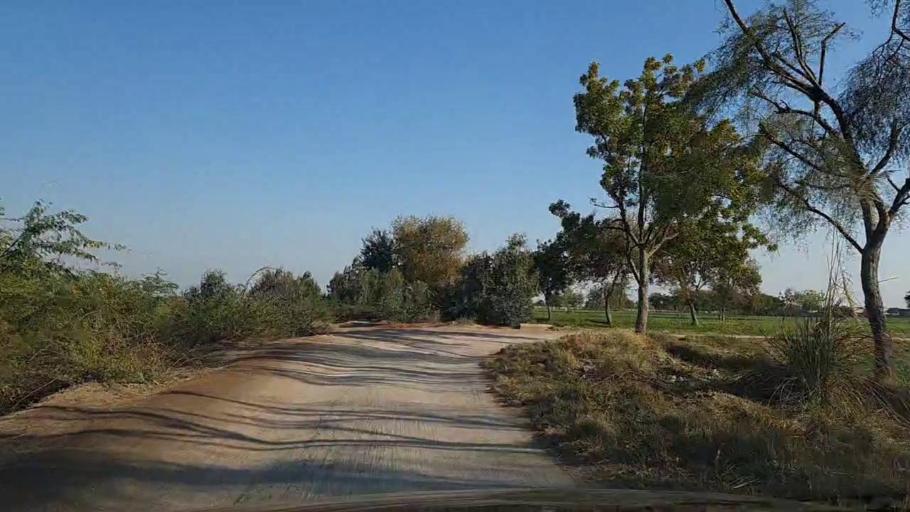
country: PK
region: Sindh
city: Nawabshah
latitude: 26.2088
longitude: 68.3749
